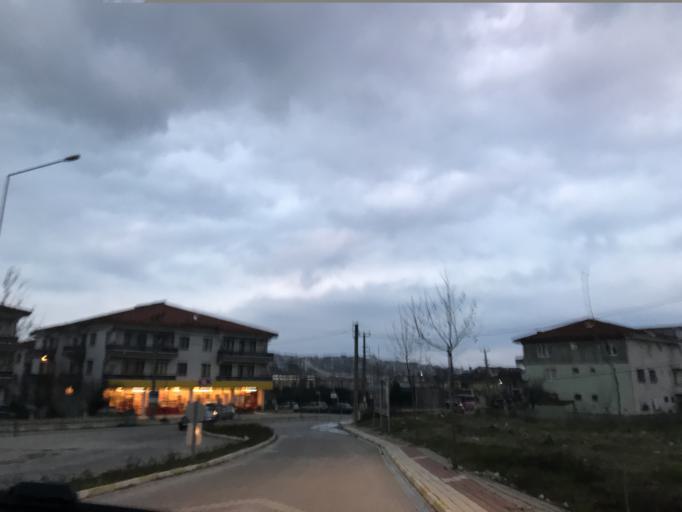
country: TR
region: Yalova
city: Yalova
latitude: 40.6380
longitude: 29.2620
